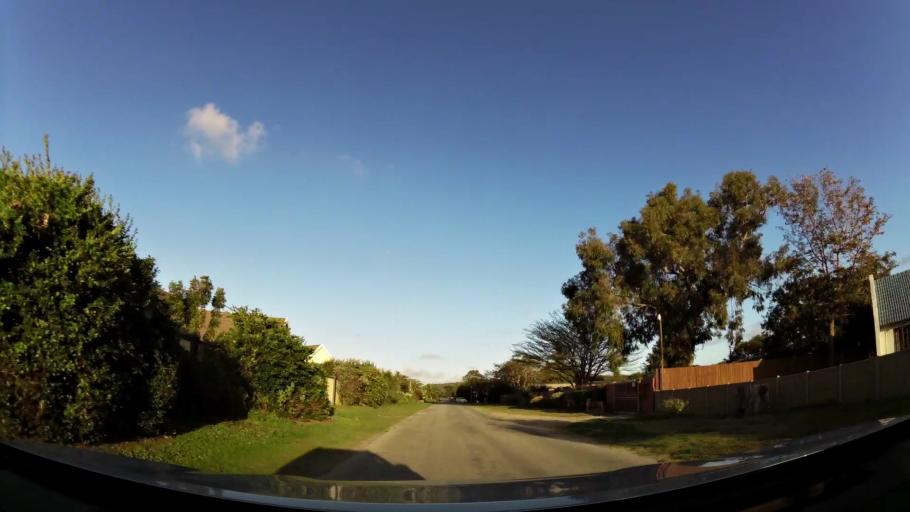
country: ZA
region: Western Cape
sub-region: Eden District Municipality
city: Knysna
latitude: -34.0125
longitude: 22.7797
